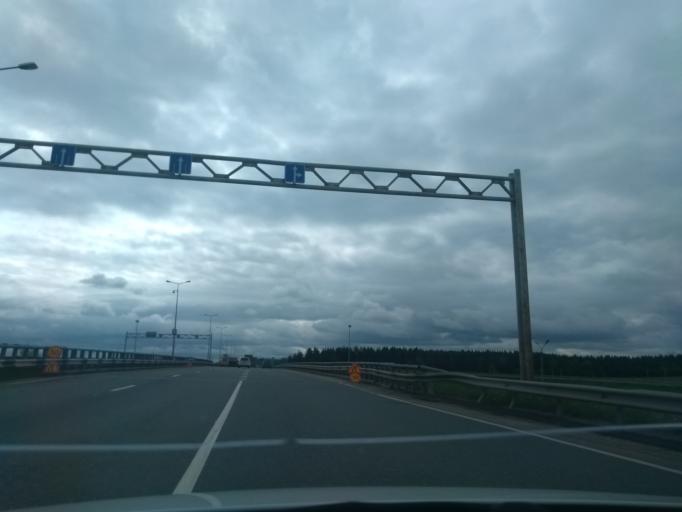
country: RU
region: Perm
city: Froly
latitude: 57.9330
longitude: 56.2692
